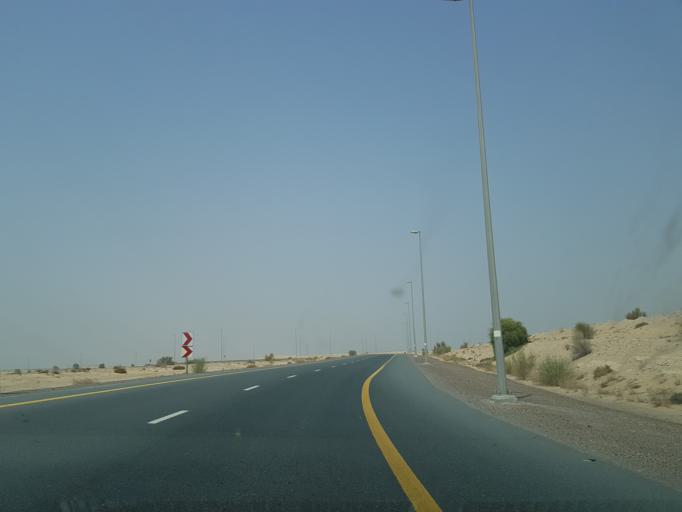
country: AE
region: Dubai
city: Dubai
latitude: 25.0514
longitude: 55.3100
